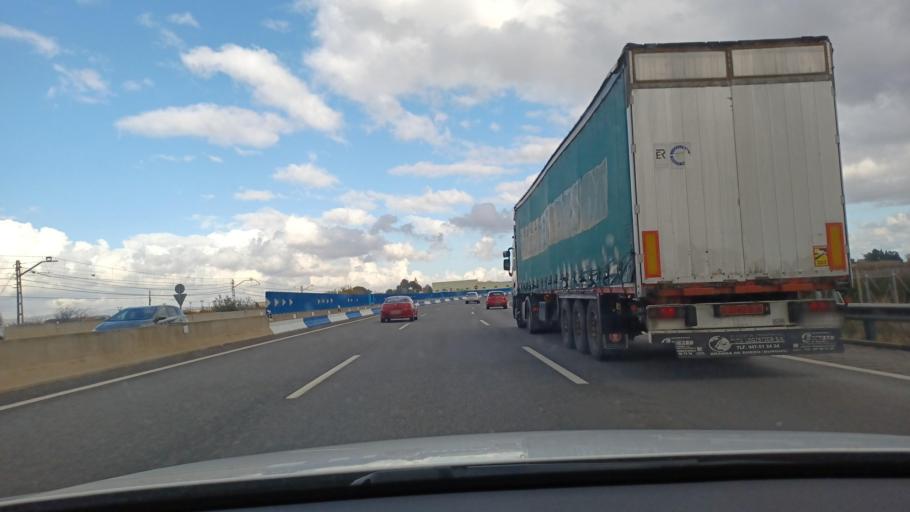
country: ES
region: Valencia
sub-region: Provincia de Valencia
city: L'Alcudia
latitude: 39.1808
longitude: -0.5133
